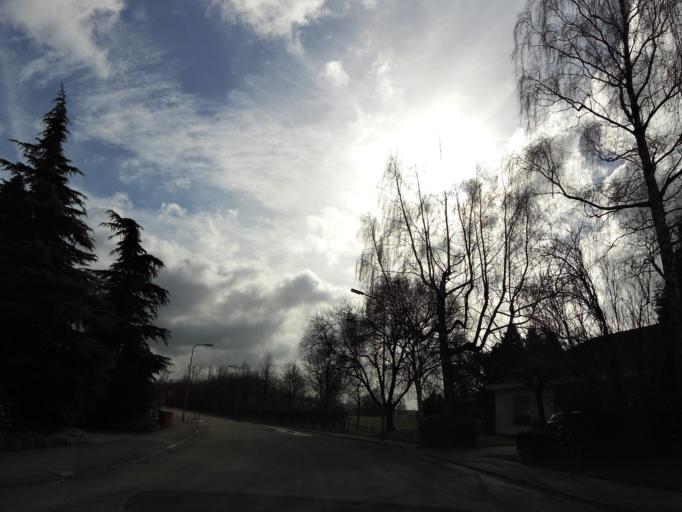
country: NL
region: Limburg
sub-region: Gemeente Meerssen
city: Meerssen
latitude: 50.8946
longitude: 5.7063
